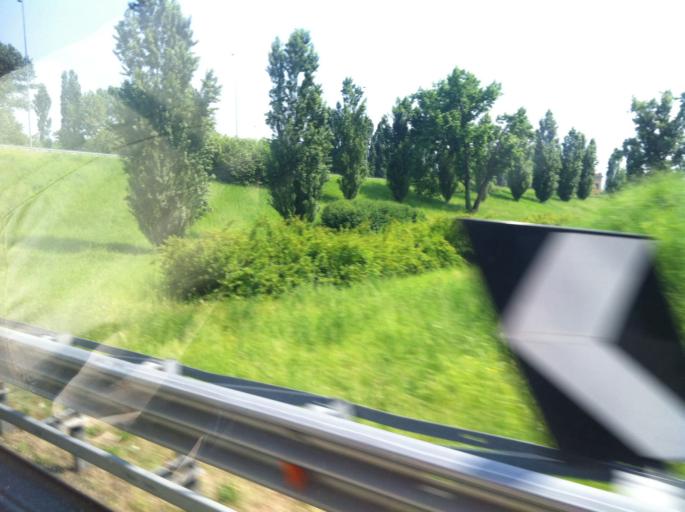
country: IT
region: Lombardy
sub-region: Citta metropolitana di Milano
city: Linate
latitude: 45.4607
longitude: 9.2509
